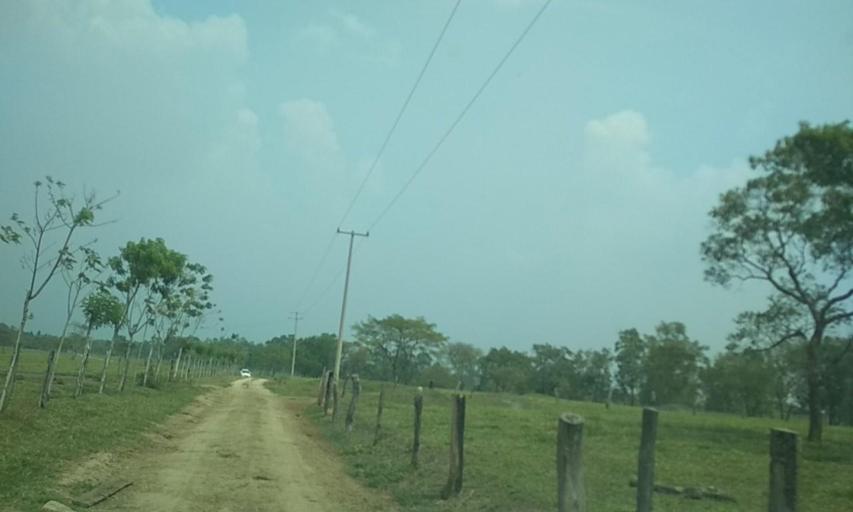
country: MX
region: Veracruz
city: Las Choapas
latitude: 17.8187
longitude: -94.0694
